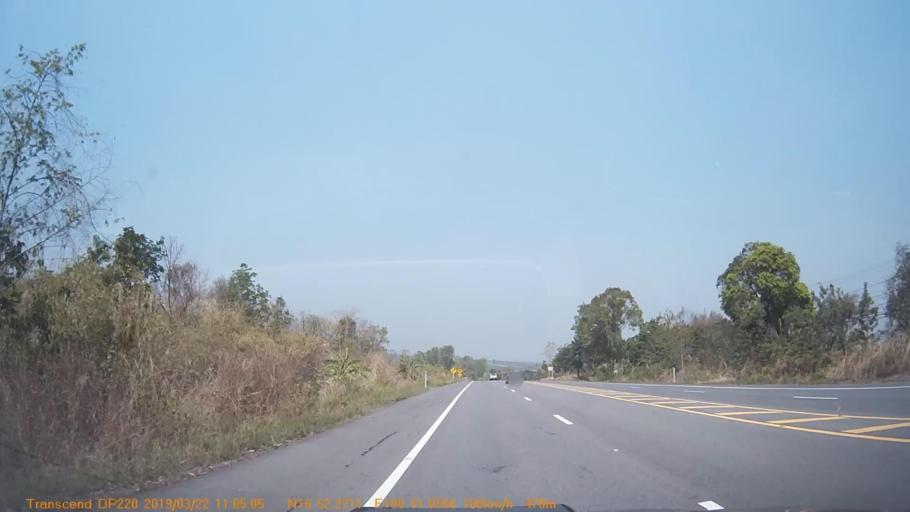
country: TH
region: Phitsanulok
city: Nakhon Thai
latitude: 16.8713
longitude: 100.8507
